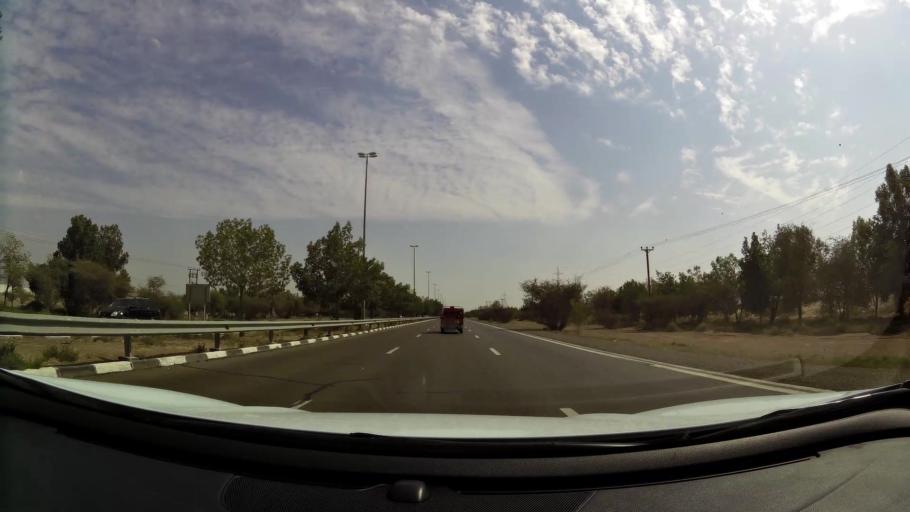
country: AE
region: Abu Dhabi
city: Al Ain
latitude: 24.1372
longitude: 55.8163
